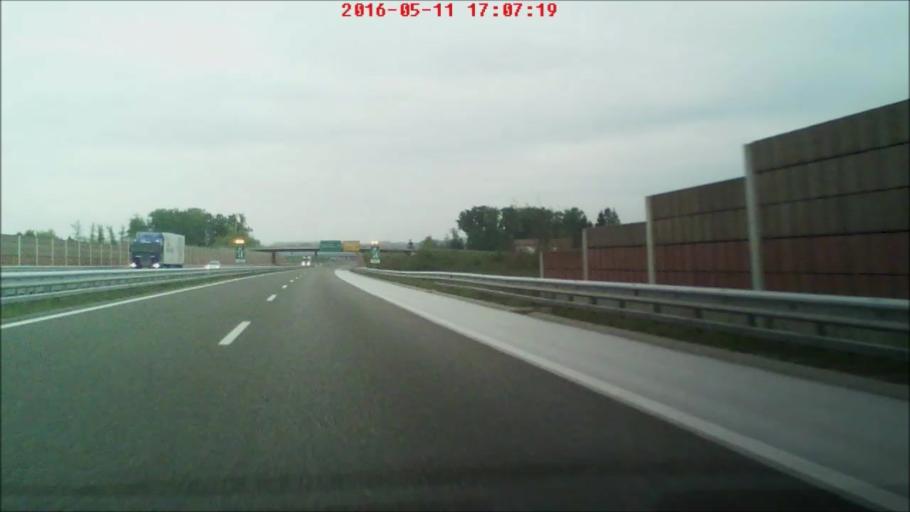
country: SI
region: Hajdina
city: Spodnja Hajdina
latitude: 46.3964
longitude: 15.8488
